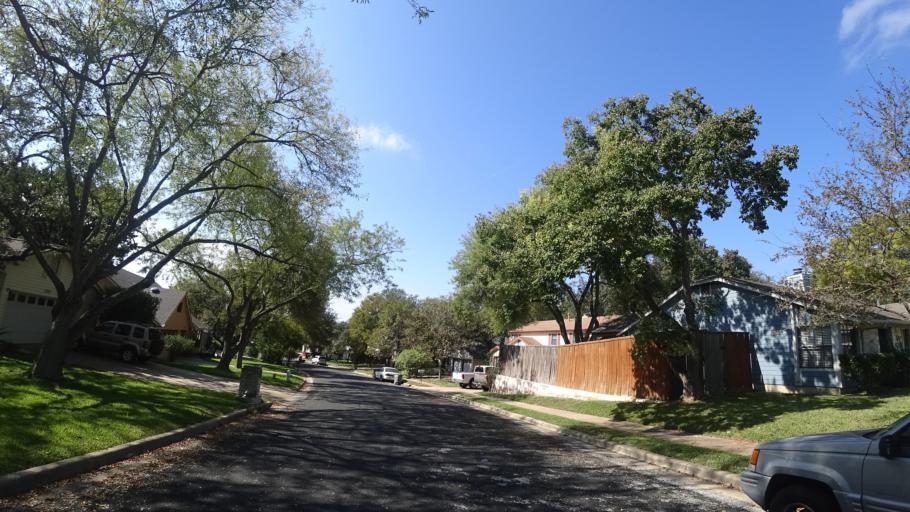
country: US
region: Texas
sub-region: Travis County
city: Shady Hollow
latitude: 30.1976
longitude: -97.8172
